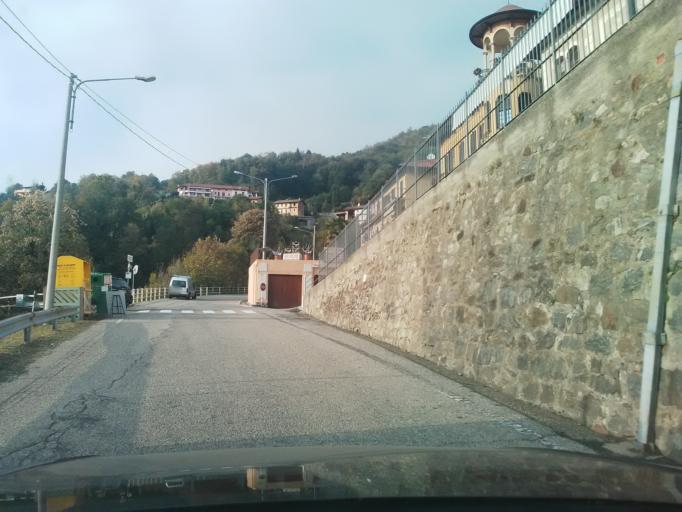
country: IT
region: Piedmont
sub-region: Provincia di Biella
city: Zumaglia
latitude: 45.6029
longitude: 8.0795
